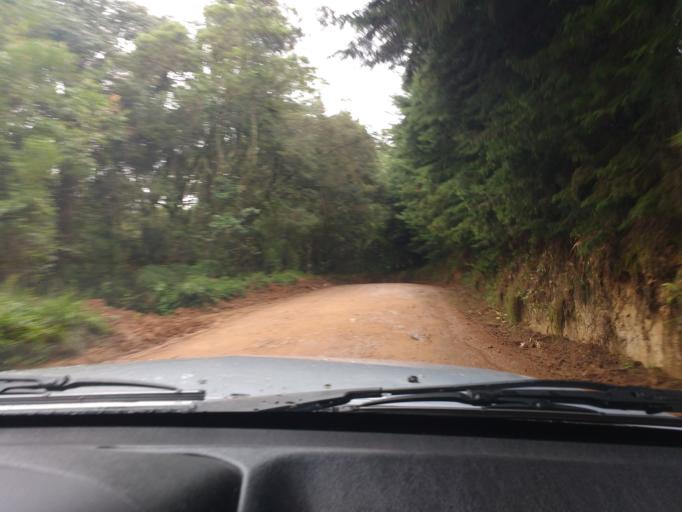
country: BR
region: Minas Gerais
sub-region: Cambui
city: Cambui
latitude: -22.7421
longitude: -45.9153
